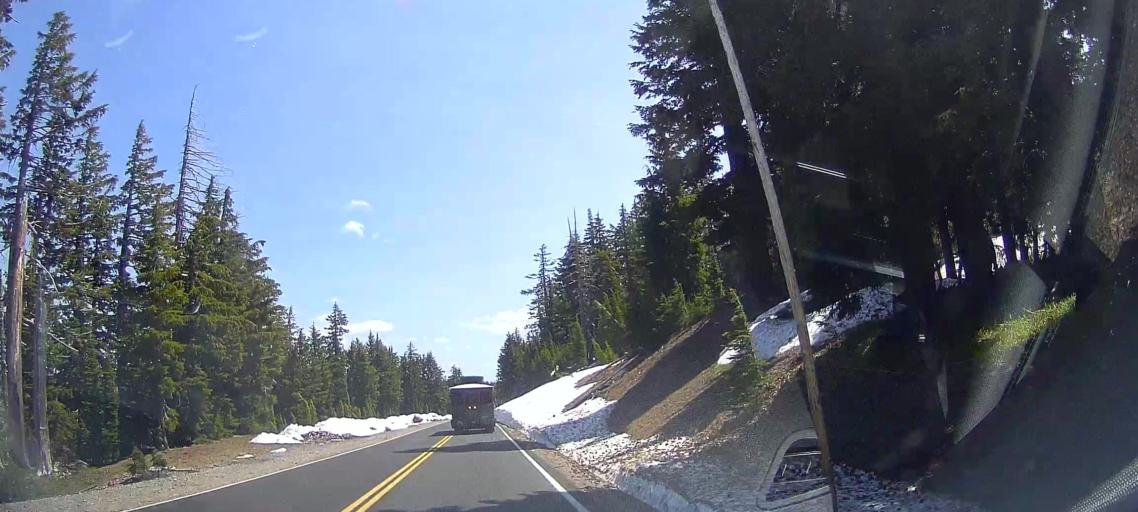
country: US
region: Oregon
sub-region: Jackson County
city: Shady Cove
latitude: 42.9807
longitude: -122.1385
